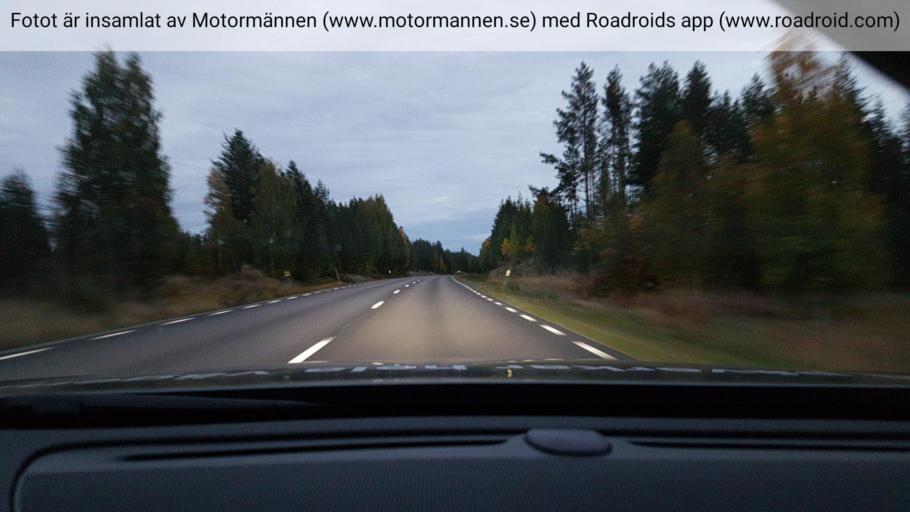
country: SE
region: Norrbotten
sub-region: Alvsbyns Kommun
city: AElvsbyn
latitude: 65.7380
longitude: 20.9689
